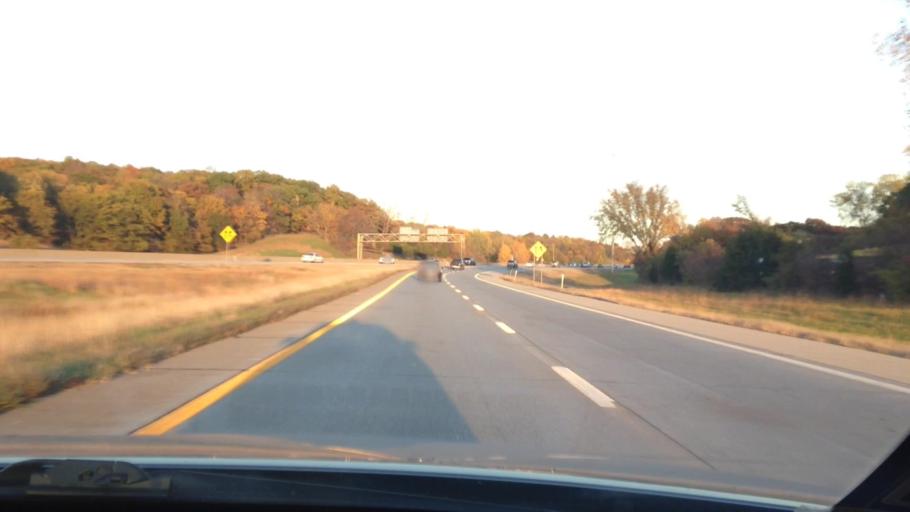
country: US
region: Kansas
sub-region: Wyandotte County
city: Edwardsville
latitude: 39.1055
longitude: -94.8037
